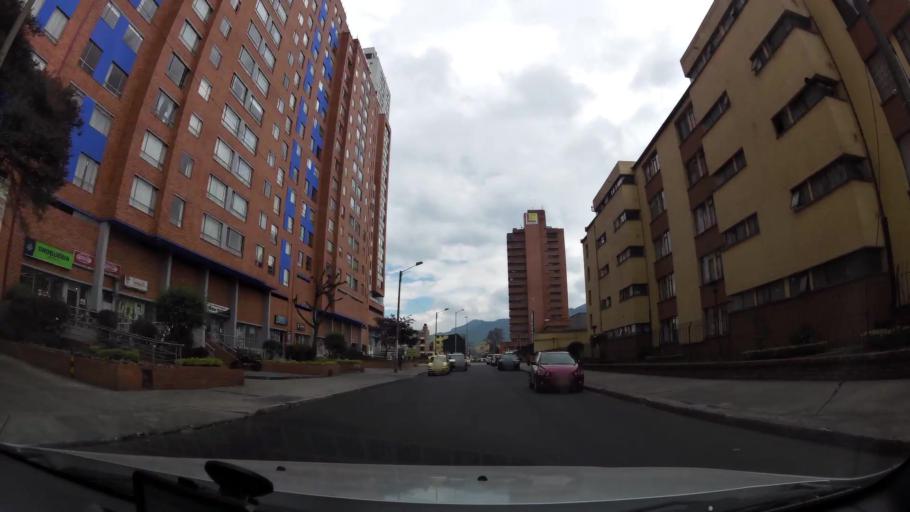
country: CO
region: Bogota D.C.
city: Bogota
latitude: 4.6287
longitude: -74.0835
